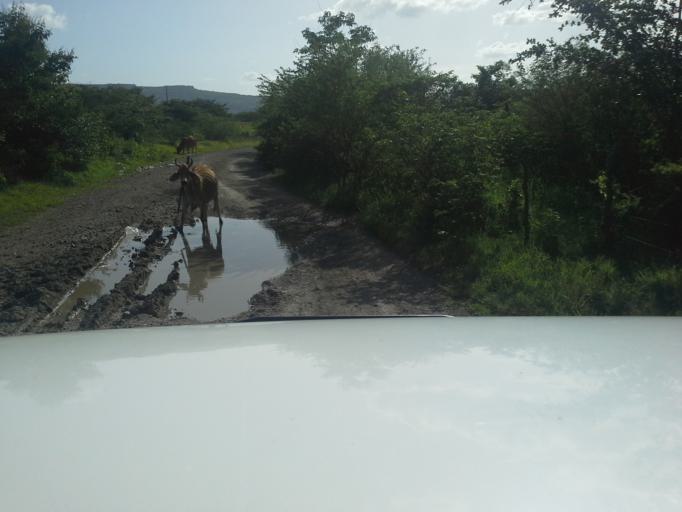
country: NI
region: Matagalpa
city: Ciudad Dario
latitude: 12.6581
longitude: -86.0788
